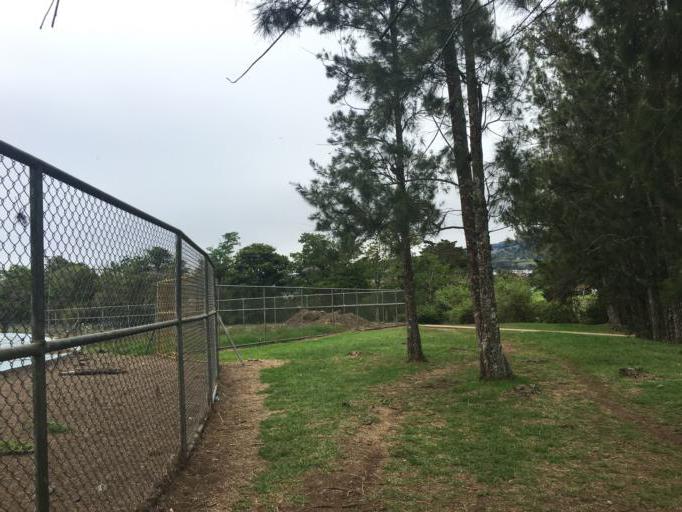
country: CR
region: Cartago
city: Cartago
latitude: 9.8562
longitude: -83.9086
